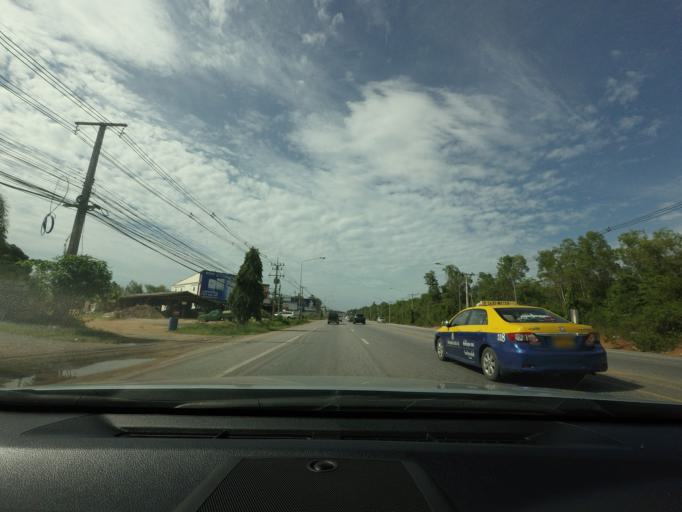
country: TH
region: Songkhla
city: Hat Yai
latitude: 6.9616
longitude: 100.4244
